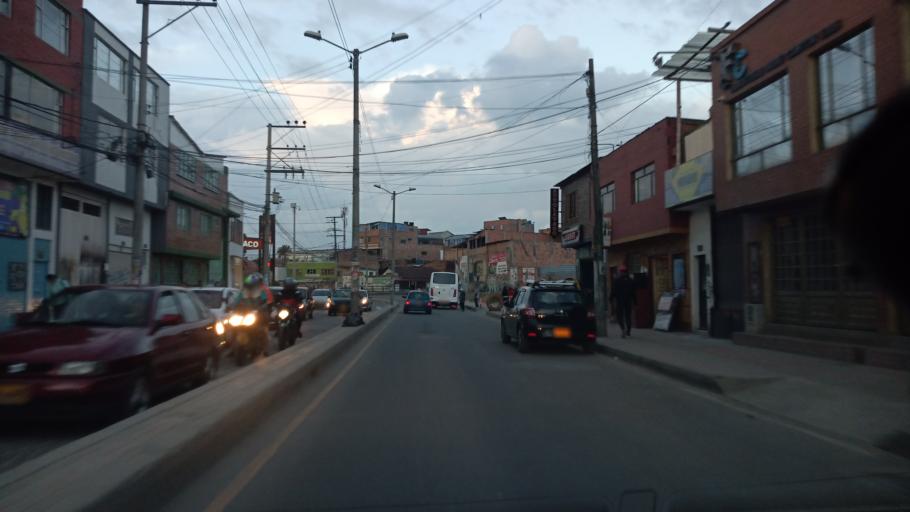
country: CO
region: Cundinamarca
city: Soacha
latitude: 4.5801
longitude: -74.2218
